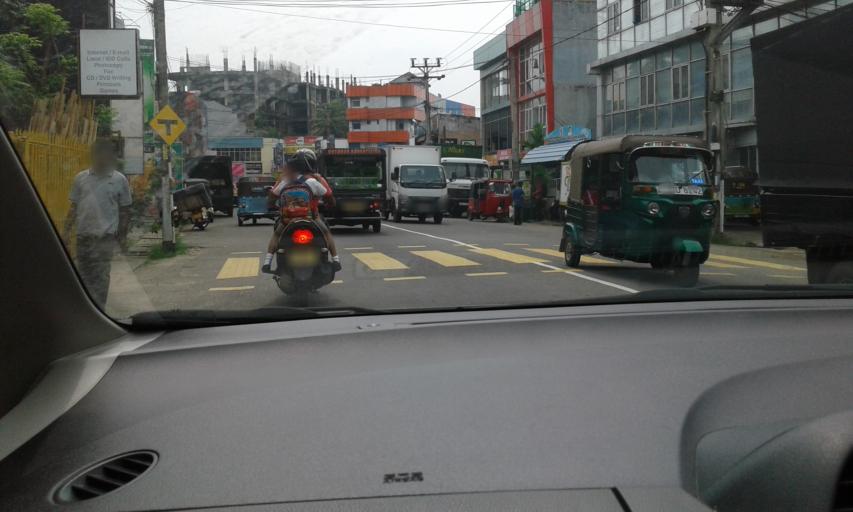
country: LK
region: Western
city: Sri Jayewardenepura Kotte
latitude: 6.8683
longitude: 79.9104
